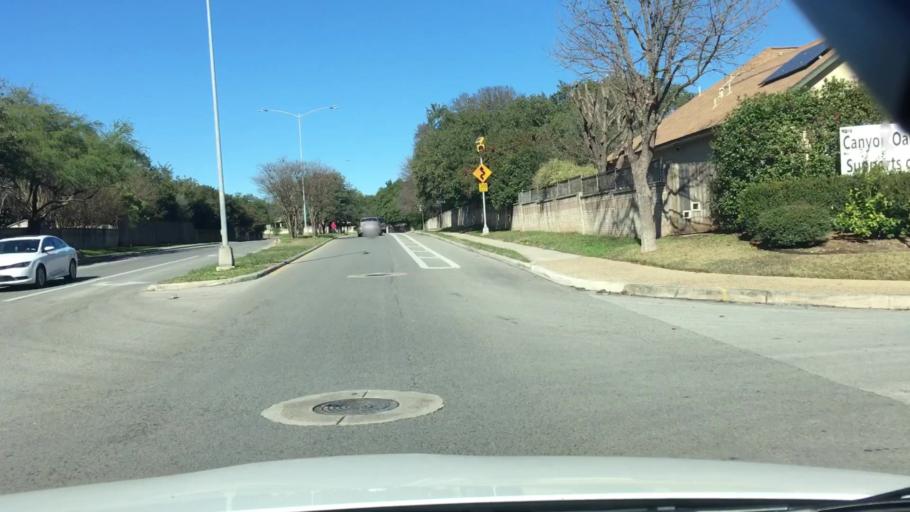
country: US
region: Texas
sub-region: Bexar County
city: Hollywood Park
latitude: 29.5960
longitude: -98.4540
